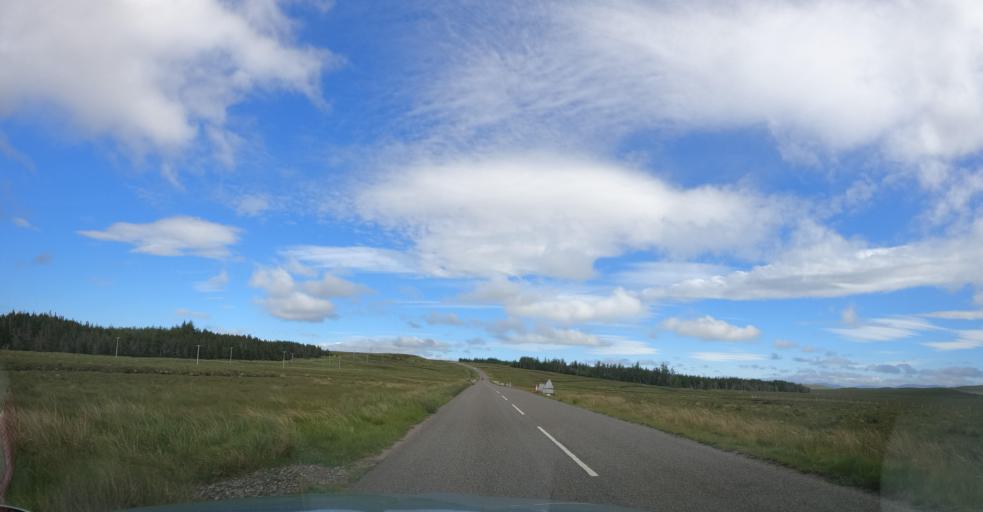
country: GB
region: Scotland
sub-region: Eilean Siar
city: Isle of Lewis
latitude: 58.1824
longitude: -6.6672
